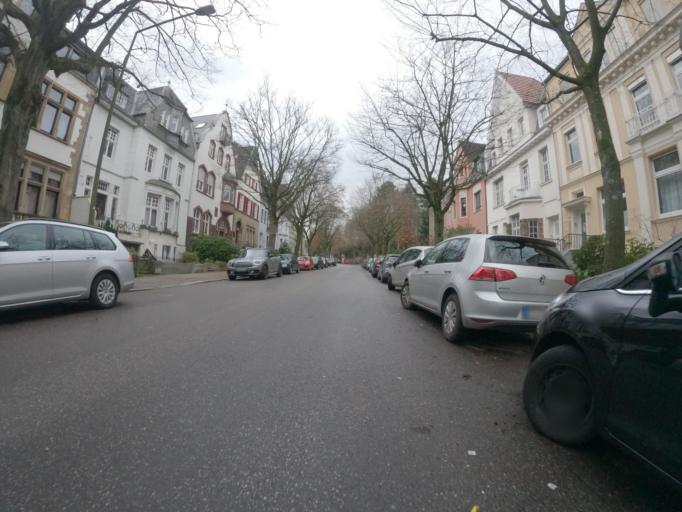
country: DE
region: North Rhine-Westphalia
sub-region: Regierungsbezirk Koln
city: Aachen
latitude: 50.7624
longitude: 6.0814
